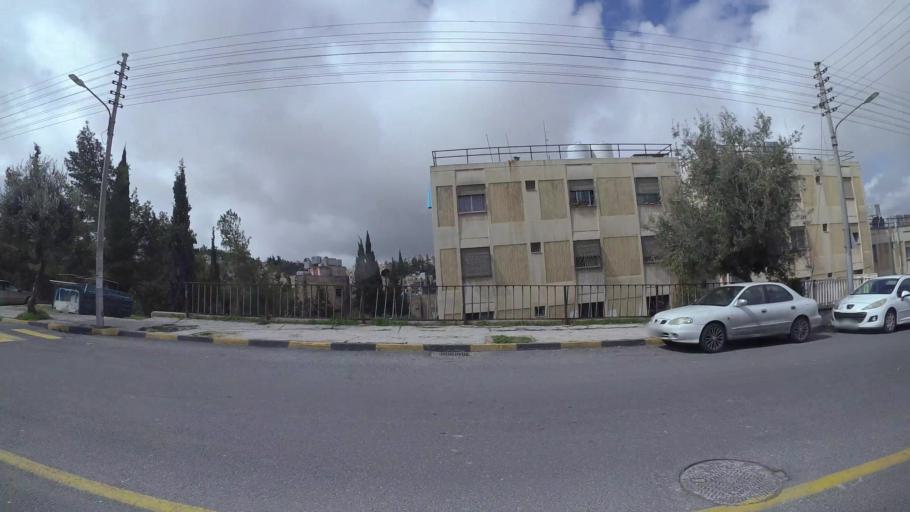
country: JO
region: Amman
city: Al Jubayhah
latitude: 32.0599
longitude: 35.8843
